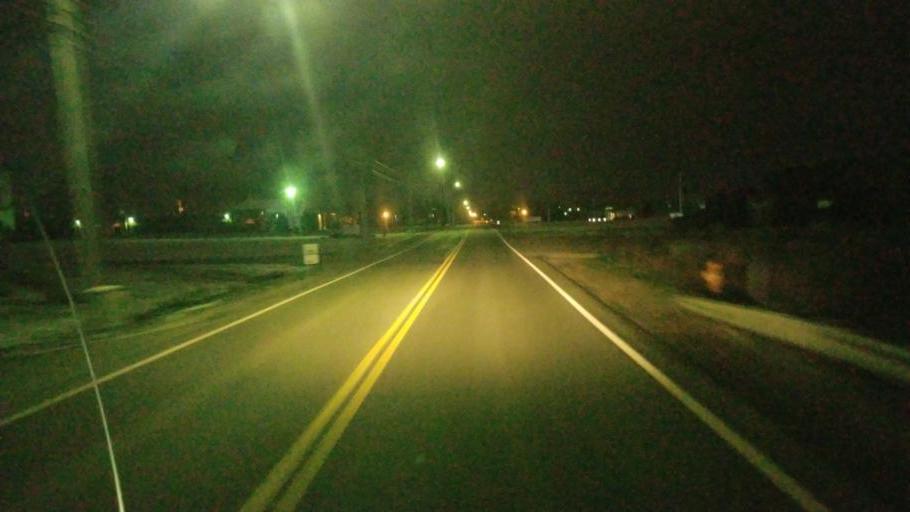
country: US
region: Ohio
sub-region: Cuyahoga County
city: Solon
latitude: 41.3871
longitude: -81.4639
